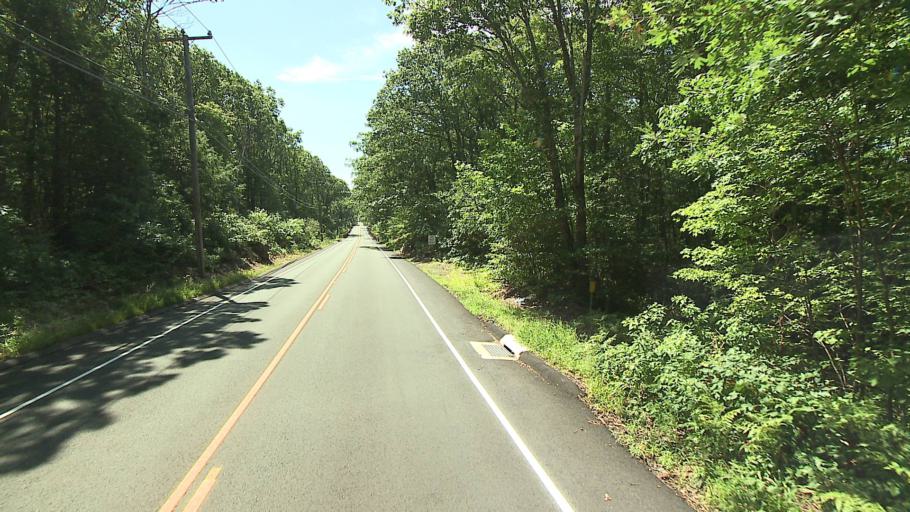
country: US
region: Connecticut
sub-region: Litchfield County
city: New Hartford Center
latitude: 41.9475
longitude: -72.9170
